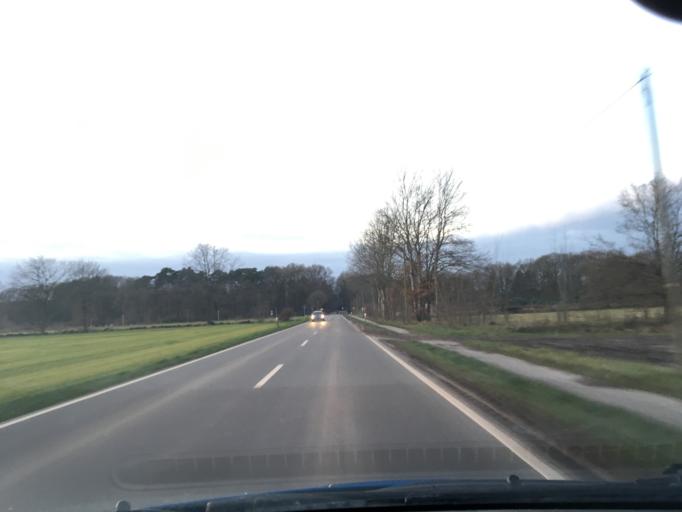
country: DE
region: Lower Saxony
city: Barum
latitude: 53.3460
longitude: 10.4227
